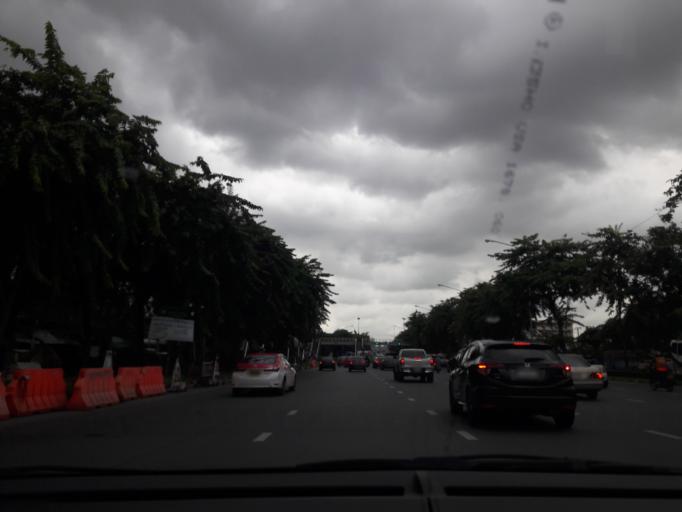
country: TH
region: Bangkok
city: Bangkok Noi
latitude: 13.7665
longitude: 100.4876
